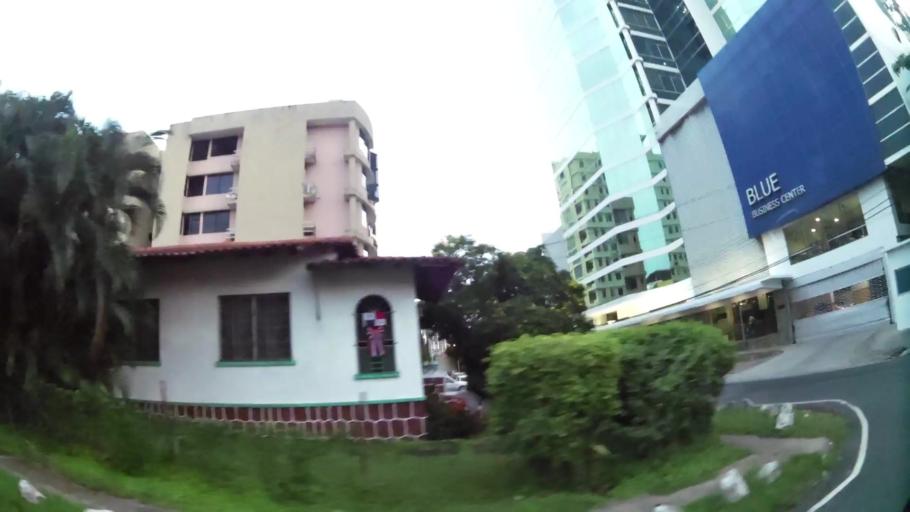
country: PA
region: Panama
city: Panama
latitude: 8.9953
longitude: -79.5121
